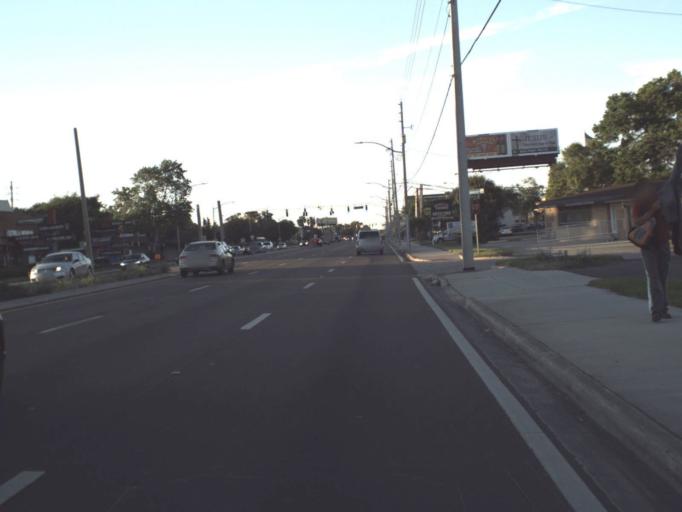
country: US
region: Florida
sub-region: Orange County
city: Azalea Park
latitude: 28.5415
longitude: -81.3105
